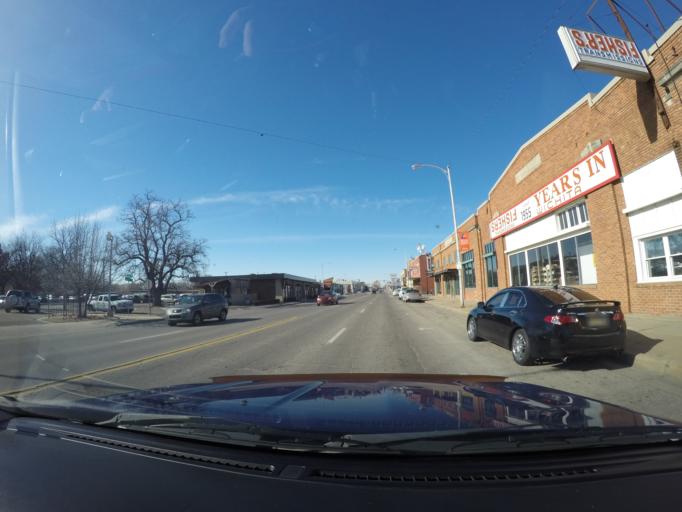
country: US
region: Kansas
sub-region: Sedgwick County
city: Wichita
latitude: 37.6862
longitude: -97.3158
